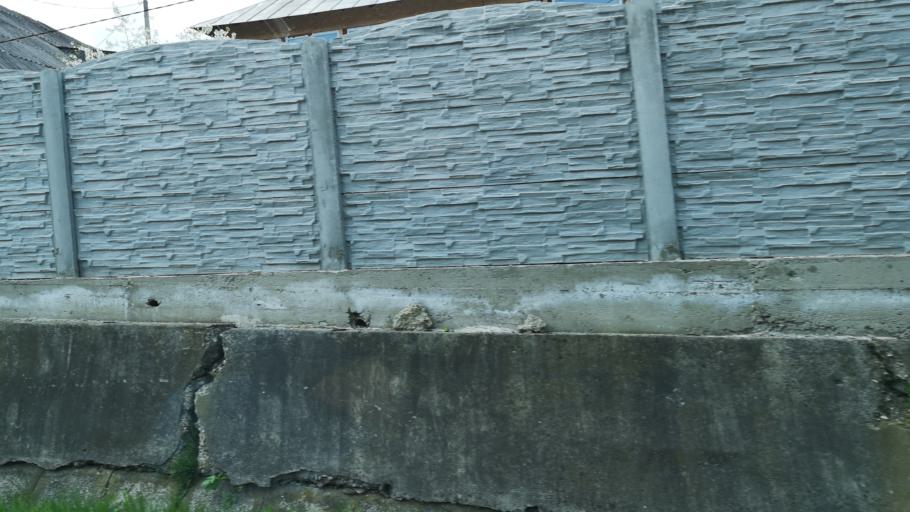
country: RO
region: Prahova
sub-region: Comuna Soimari
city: Soimari
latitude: 45.1656
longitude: 26.2105
